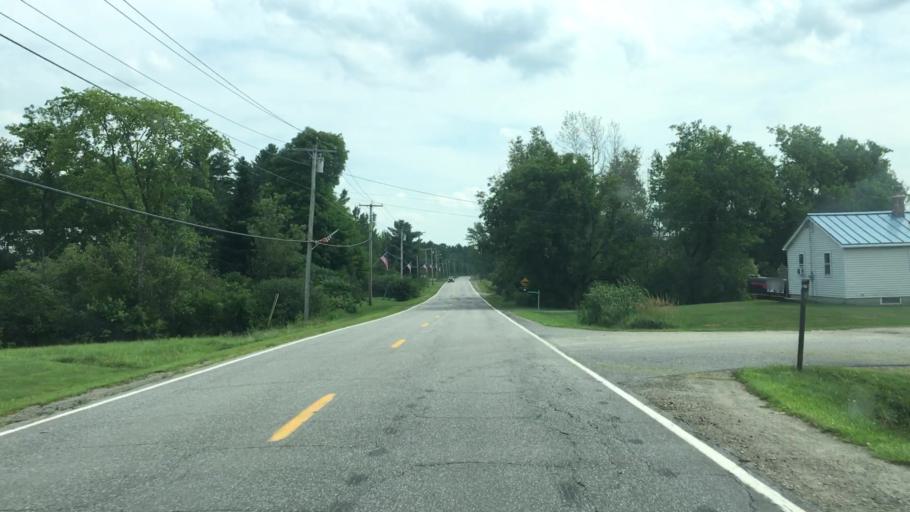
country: US
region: Maine
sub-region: Kennebec County
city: Vassalboro
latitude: 44.4725
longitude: -69.6169
